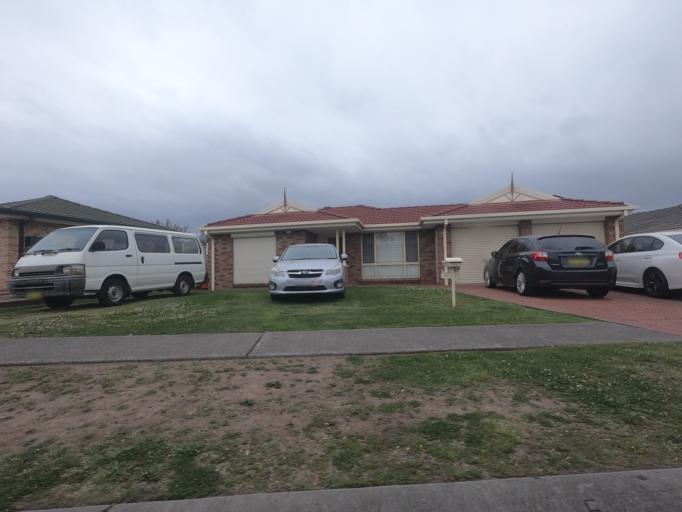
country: AU
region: New South Wales
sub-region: Wollongong
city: Dapto
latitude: -34.4879
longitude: 150.7741
